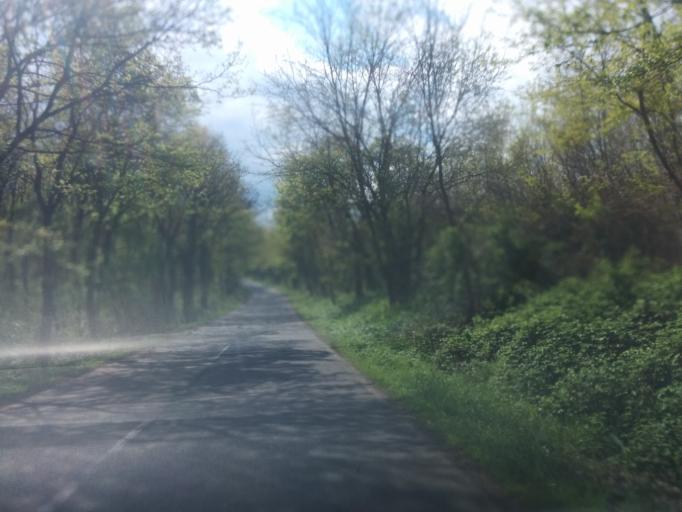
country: HU
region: Pest
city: Acsa
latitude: 47.8441
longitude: 19.3328
